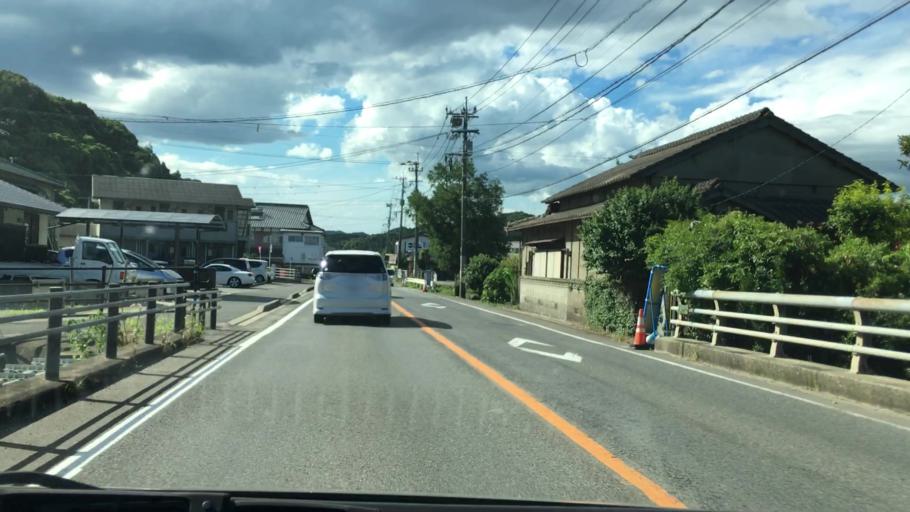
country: JP
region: Saga Prefecture
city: Takeocho-takeo
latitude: 33.1909
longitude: 129.9831
